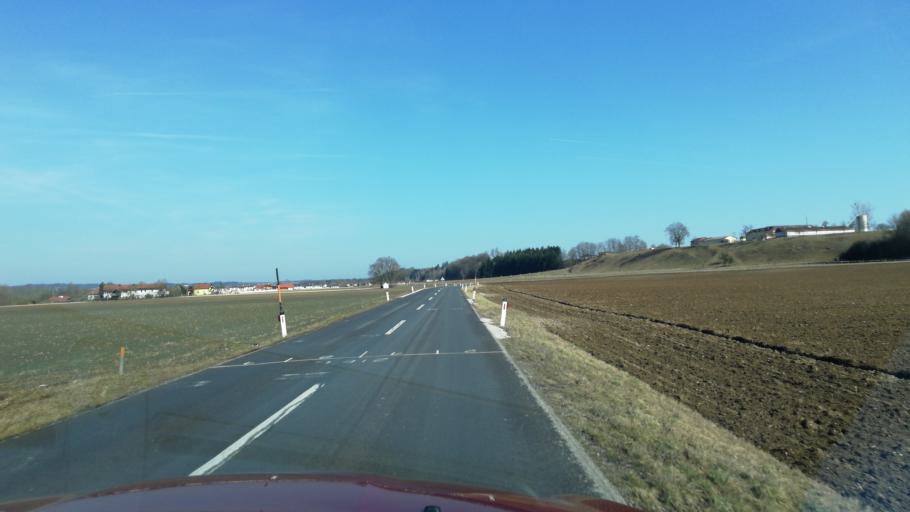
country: AT
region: Upper Austria
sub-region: Politischer Bezirk Vocklabruck
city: Rustorf
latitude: 48.0454
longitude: 13.7965
